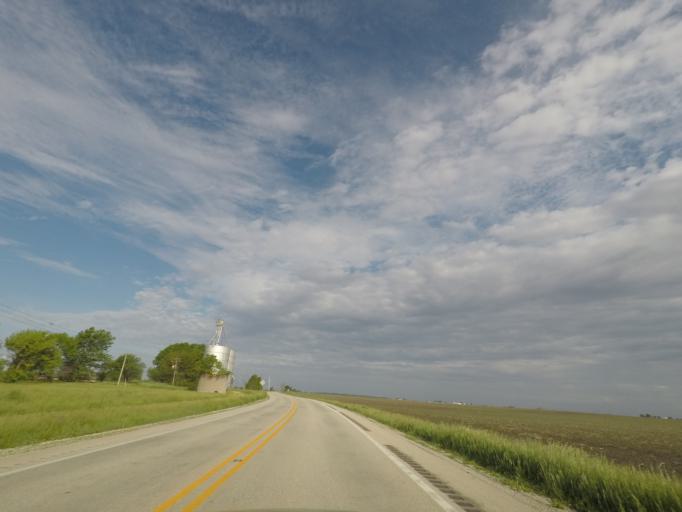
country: US
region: Illinois
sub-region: Logan County
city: Mount Pulaski
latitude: 39.9845
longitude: -89.2194
